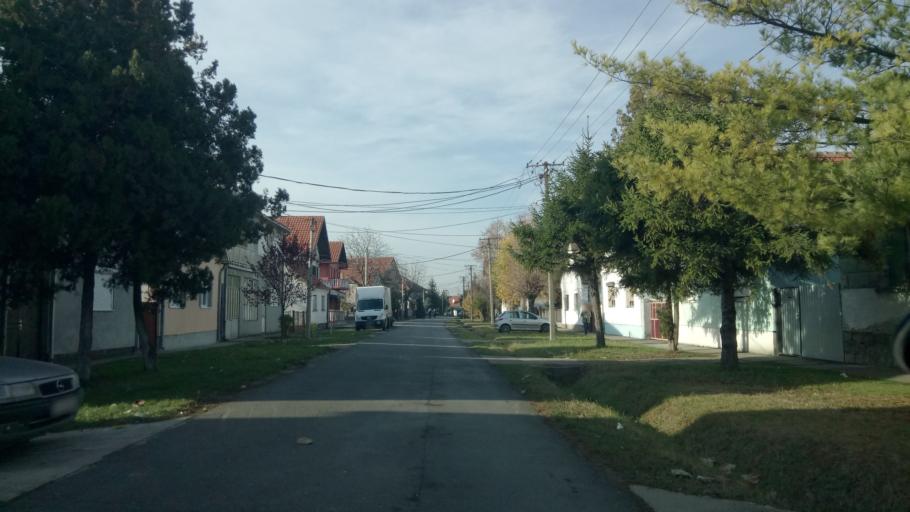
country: RS
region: Autonomna Pokrajina Vojvodina
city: Nova Pazova
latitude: 44.9497
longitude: 20.2199
